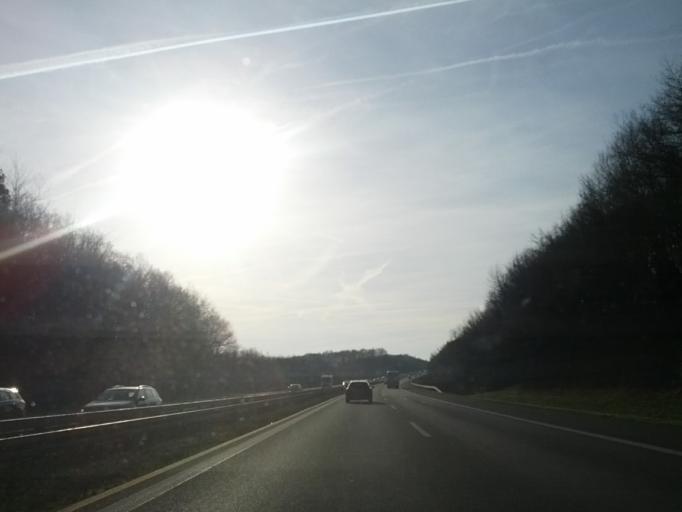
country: DE
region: Bavaria
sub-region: Regierungsbezirk Unterfranken
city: Unterpleichfeld
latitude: 49.8921
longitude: 10.0006
